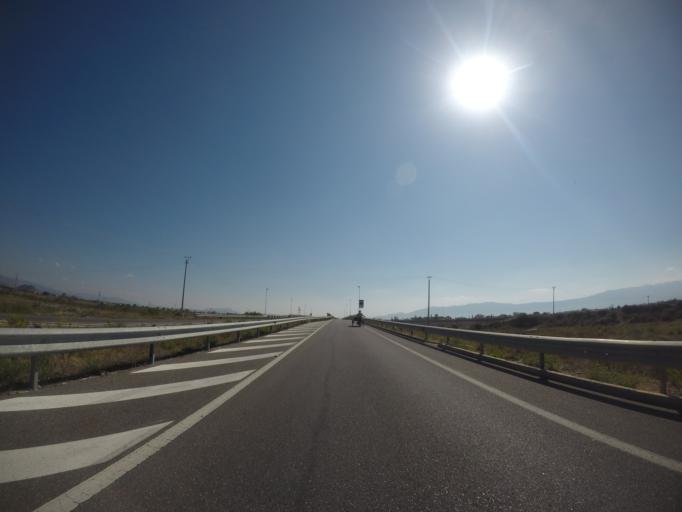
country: AL
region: Shkoder
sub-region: Rrethi i Malesia e Madhe
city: Grude-Fushe
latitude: 42.1736
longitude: 19.4650
